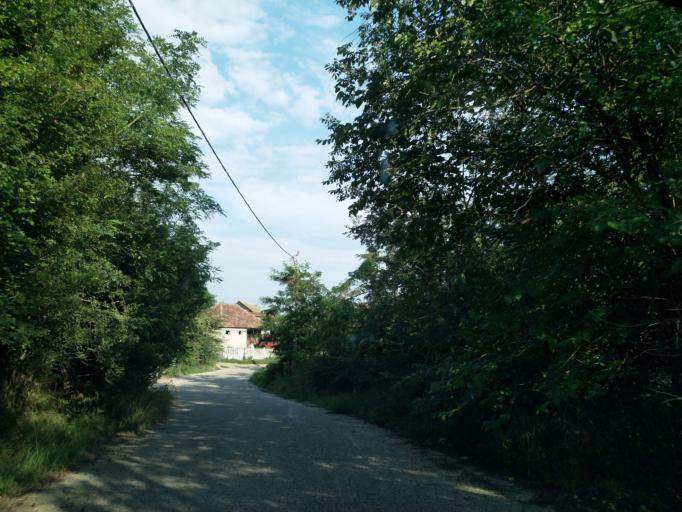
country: RS
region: Central Serbia
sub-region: Pomoravski Okrug
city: Jagodina
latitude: 44.0039
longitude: 21.1832
